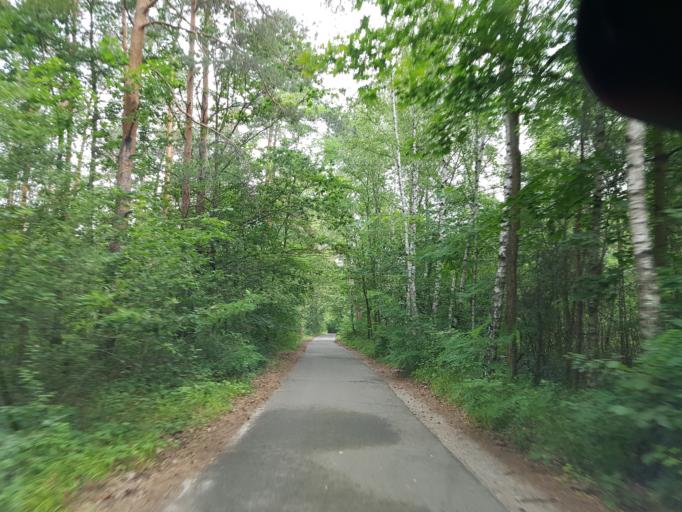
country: DE
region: Brandenburg
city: Sallgast
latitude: 51.5773
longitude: 13.8613
